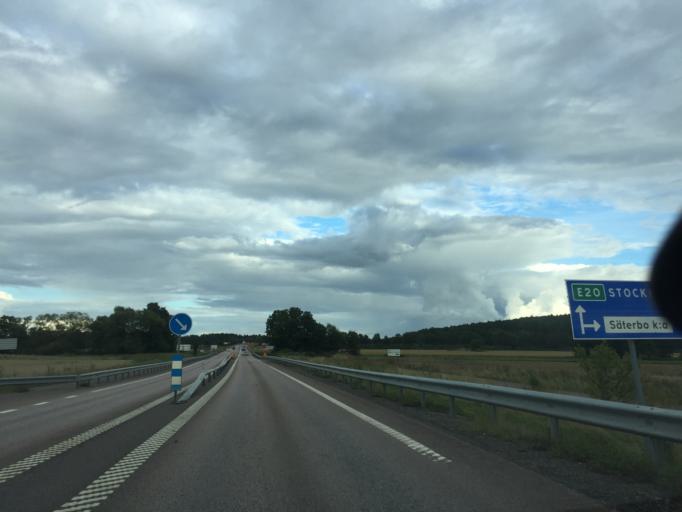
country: SE
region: Vaestmanland
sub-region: Arboga Kommun
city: Tyringe
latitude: 59.3984
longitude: 15.9191
